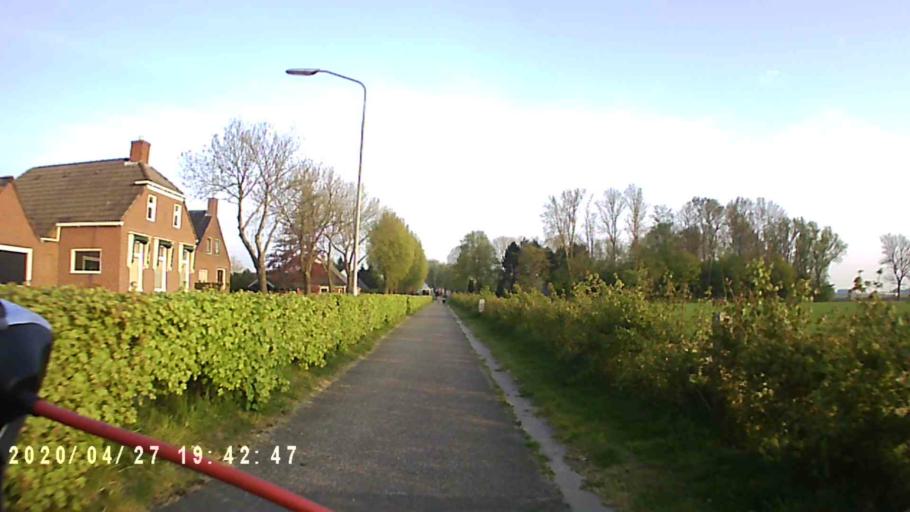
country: NL
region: Groningen
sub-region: Gemeente Winsum
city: Winsum
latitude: 53.3577
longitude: 6.4642
